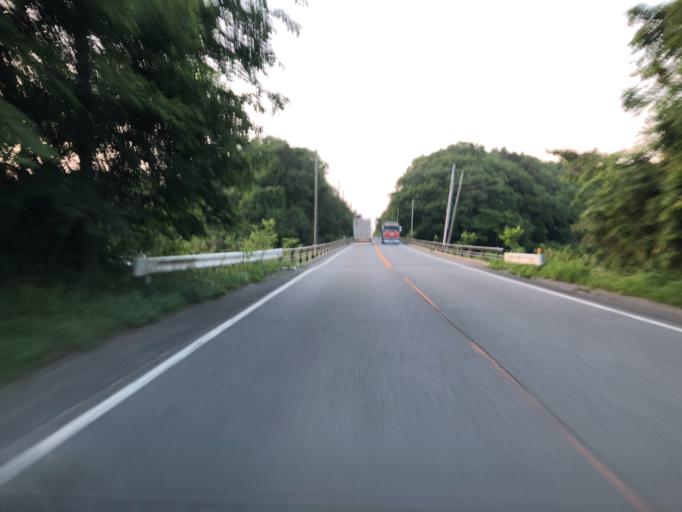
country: JP
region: Fukushima
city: Namie
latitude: 37.4733
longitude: 141.0080
